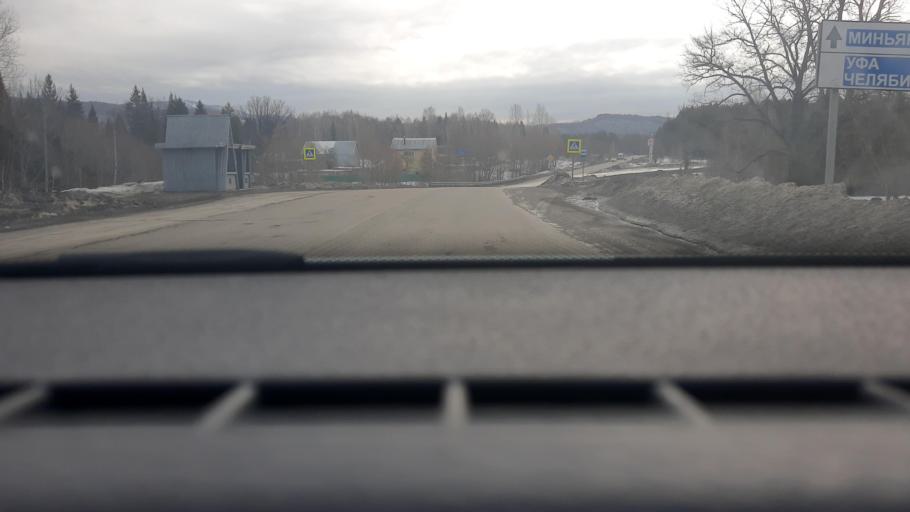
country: RU
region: Chelyabinsk
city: Asha
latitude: 54.9719
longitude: 57.2846
